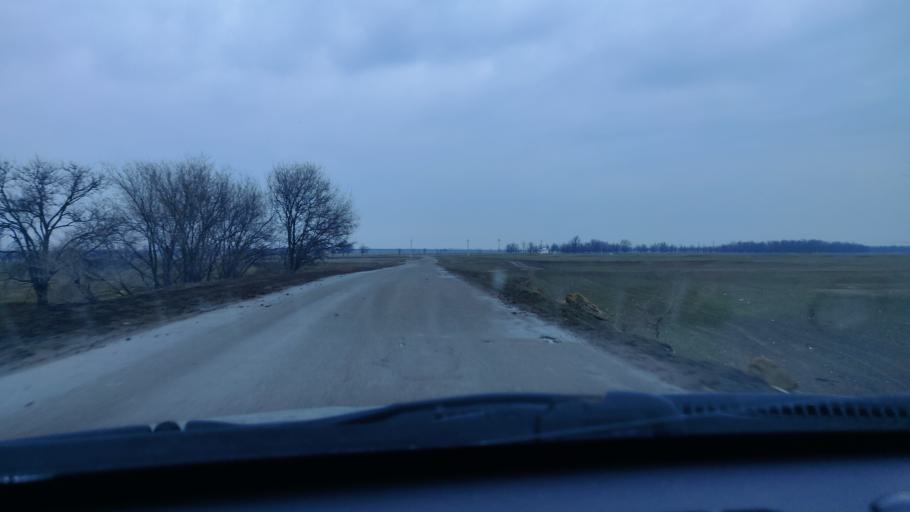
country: RU
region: Stavropol'skiy
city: Letnyaya Stavka
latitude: 45.4137
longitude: 43.7036
